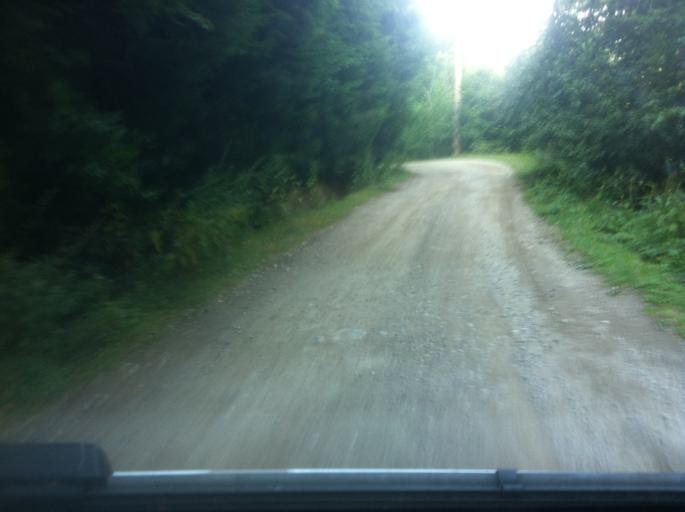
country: RO
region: Hunedoara
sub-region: Comuna Rau de Mori
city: Rau de Mori
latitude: 45.4391
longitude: 22.8920
